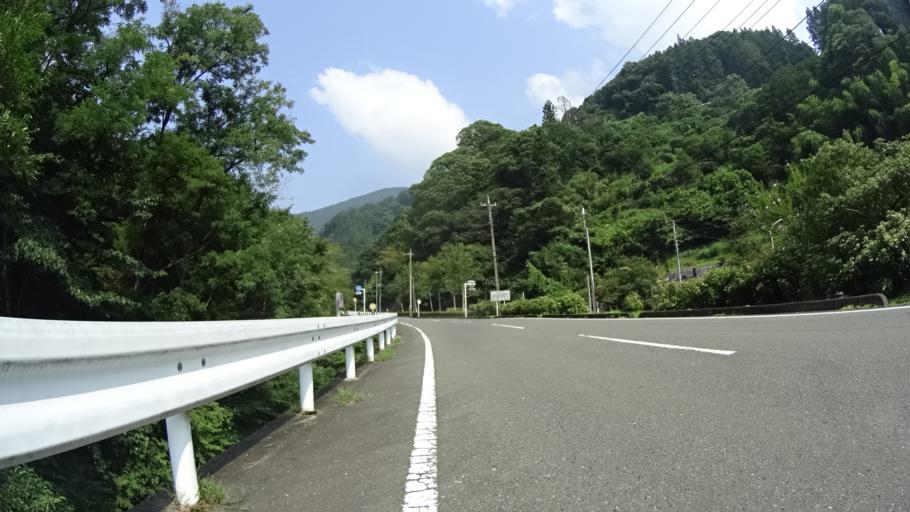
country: JP
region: Gunma
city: Tomioka
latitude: 36.0563
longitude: 138.8589
